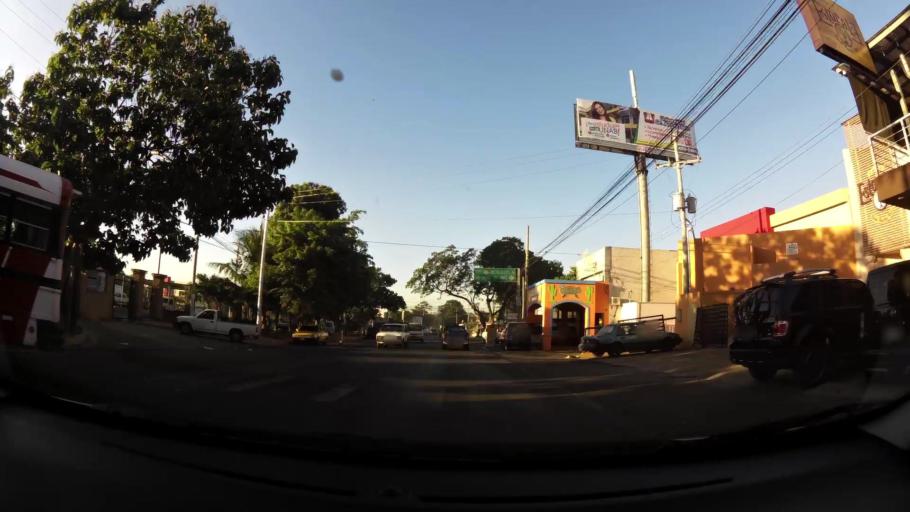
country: SV
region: Sonsonate
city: Sonsonate
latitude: 13.7107
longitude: -89.7281
